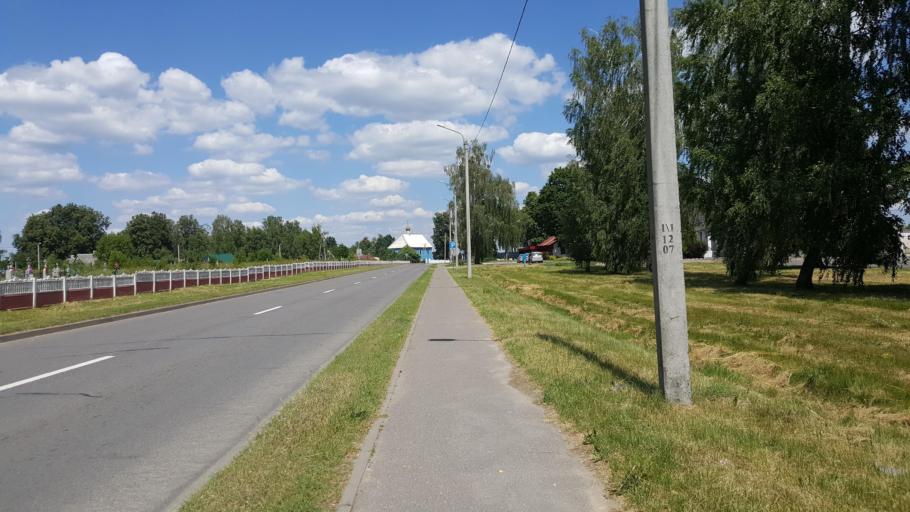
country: BY
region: Brest
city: Kamyanyuki
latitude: 52.4889
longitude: 23.7784
